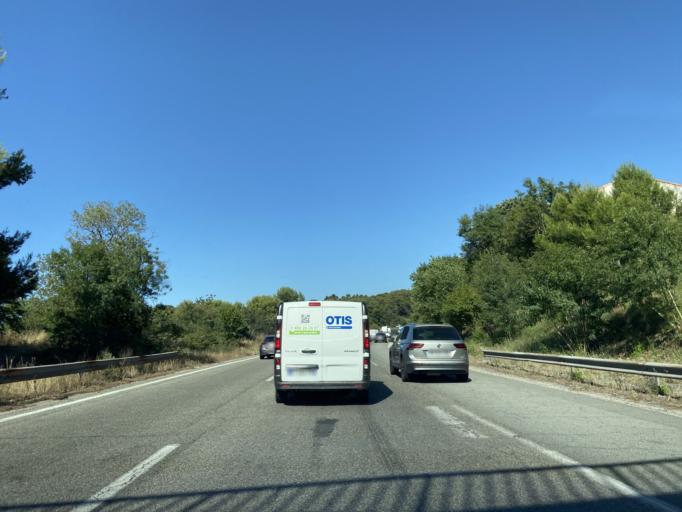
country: FR
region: Provence-Alpes-Cote d'Azur
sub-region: Departement des Bouches-du-Rhone
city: Les Pennes-Mirabeau
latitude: 43.4031
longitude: 5.3028
